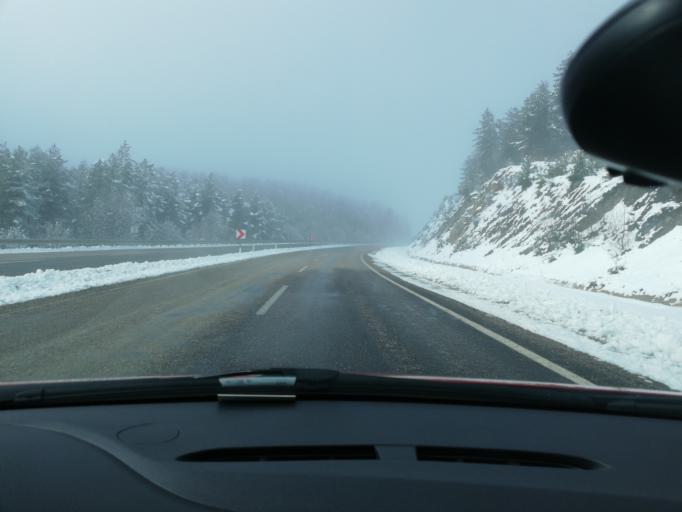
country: TR
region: Kastamonu
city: Akkaya
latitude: 41.2997
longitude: 33.5302
